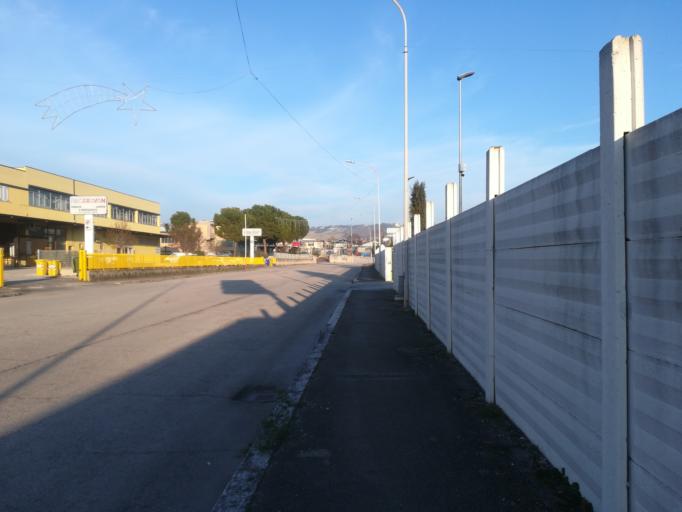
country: IT
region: The Marches
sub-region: Provincia di Macerata
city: Piediripa
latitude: 43.2777
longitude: 13.4947
